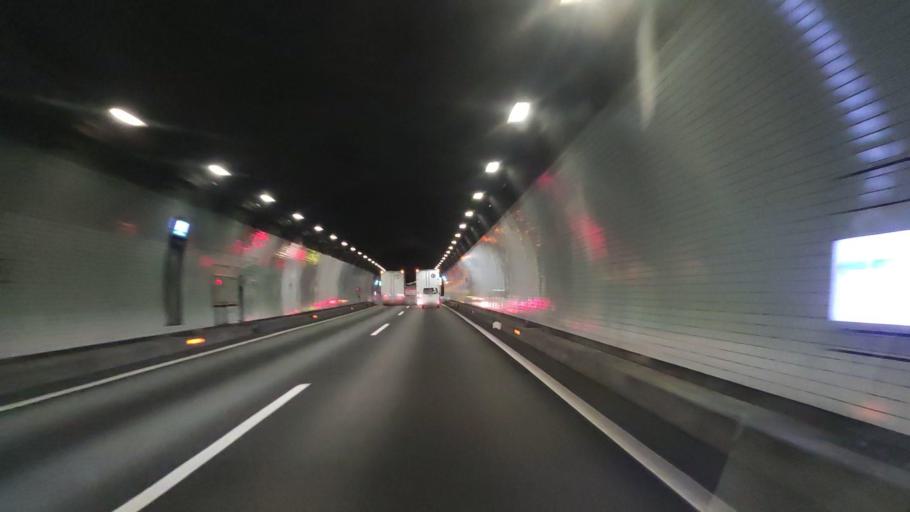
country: JP
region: Tokyo
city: Fussa
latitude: 35.7529
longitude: 139.2833
